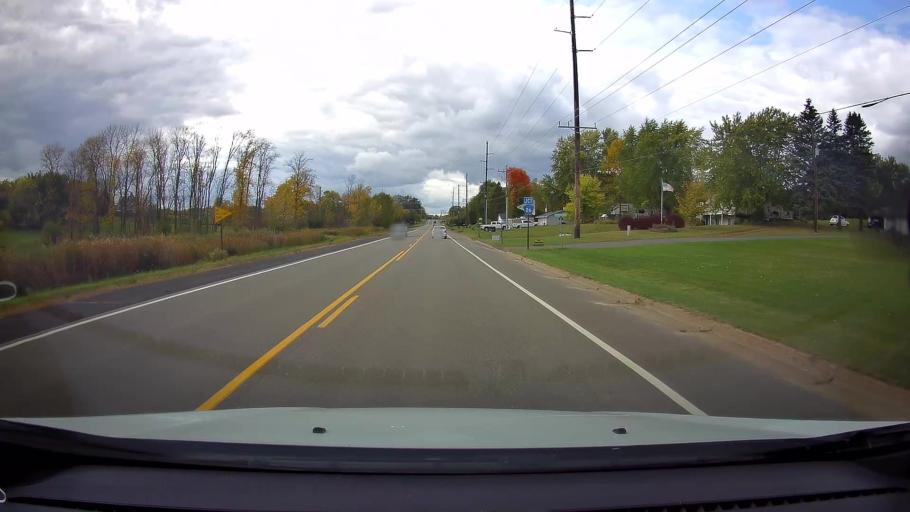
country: US
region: Minnesota
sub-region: Chisago County
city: Center City
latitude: 45.3973
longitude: -92.8018
